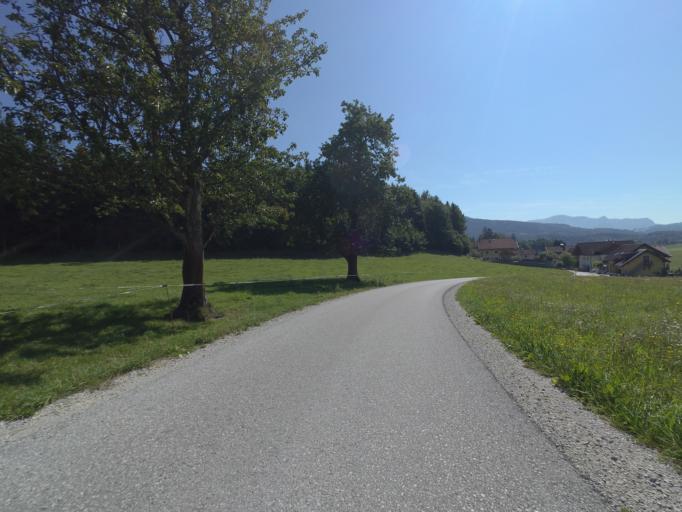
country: AT
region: Salzburg
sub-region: Politischer Bezirk Hallein
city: Adnet
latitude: 47.6813
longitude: 13.1329
